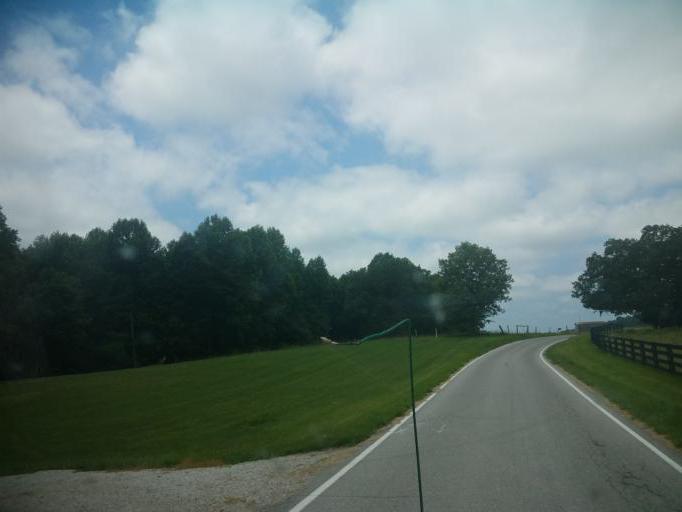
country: US
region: Kentucky
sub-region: Hart County
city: Munfordville
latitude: 37.3383
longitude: -86.0319
